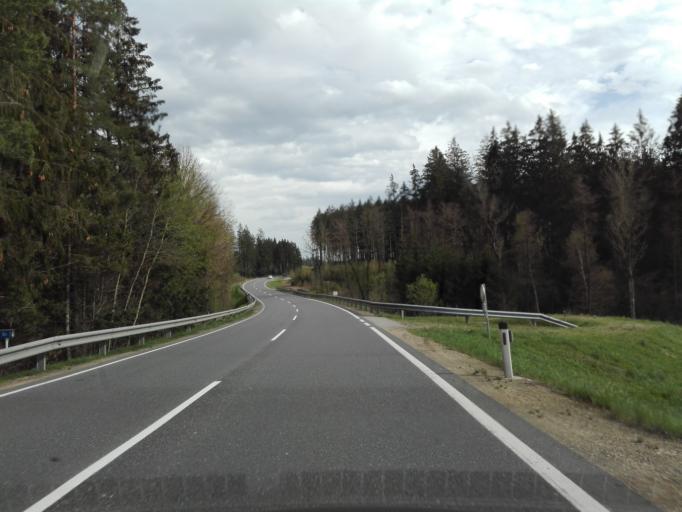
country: AT
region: Upper Austria
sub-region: Politischer Bezirk Rohrbach
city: Kleinzell im Muehlkreis
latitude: 48.4617
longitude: 14.0268
